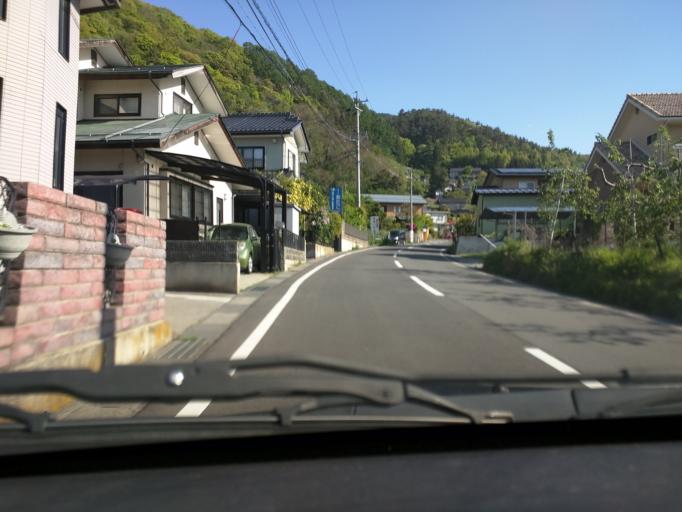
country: JP
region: Nagano
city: Nagano-shi
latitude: 36.6623
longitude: 138.1774
